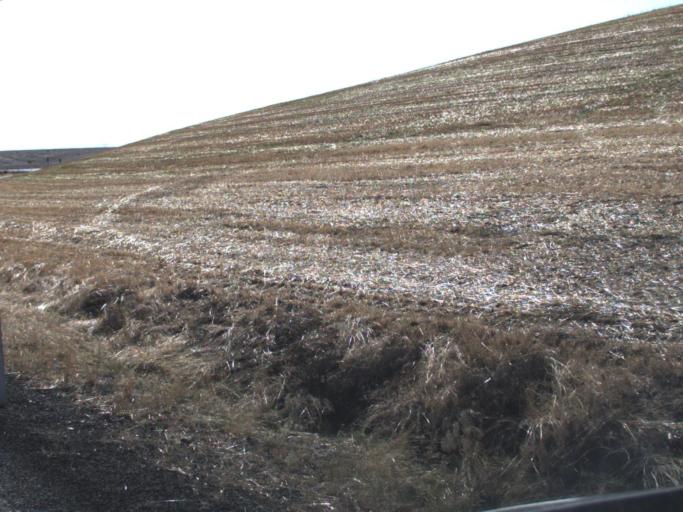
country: US
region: Washington
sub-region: Walla Walla County
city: Walla Walla
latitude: 46.1066
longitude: -118.3718
